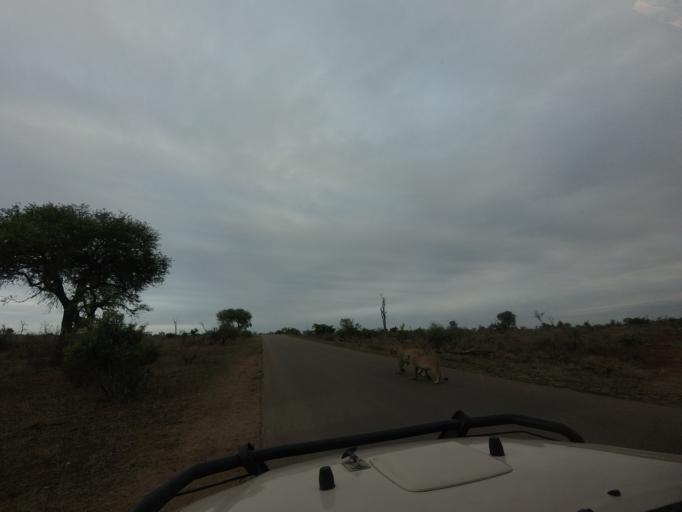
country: ZA
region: Mpumalanga
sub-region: Ehlanzeni District
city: Komatipoort
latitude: -25.3554
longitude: 31.8898
